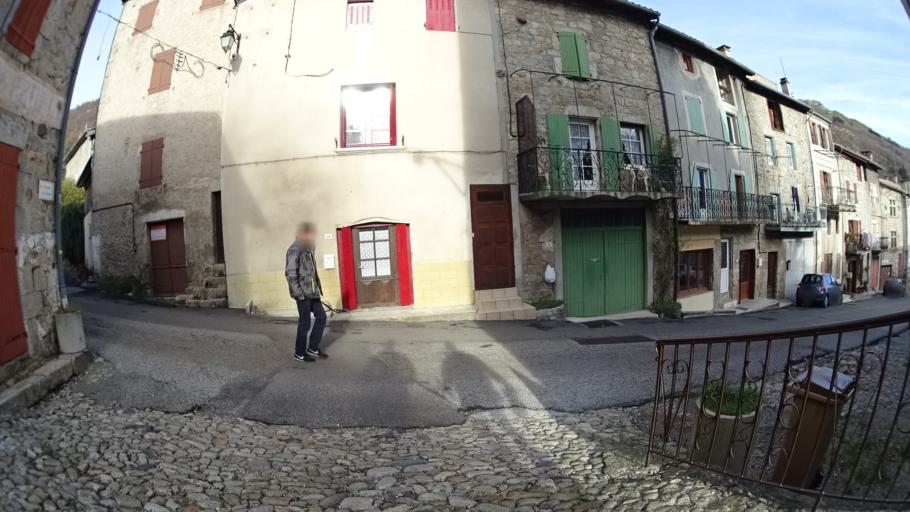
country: FR
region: Rhone-Alpes
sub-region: Departement de l'Ardeche
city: Thueyts
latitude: 44.7409
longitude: 4.2410
